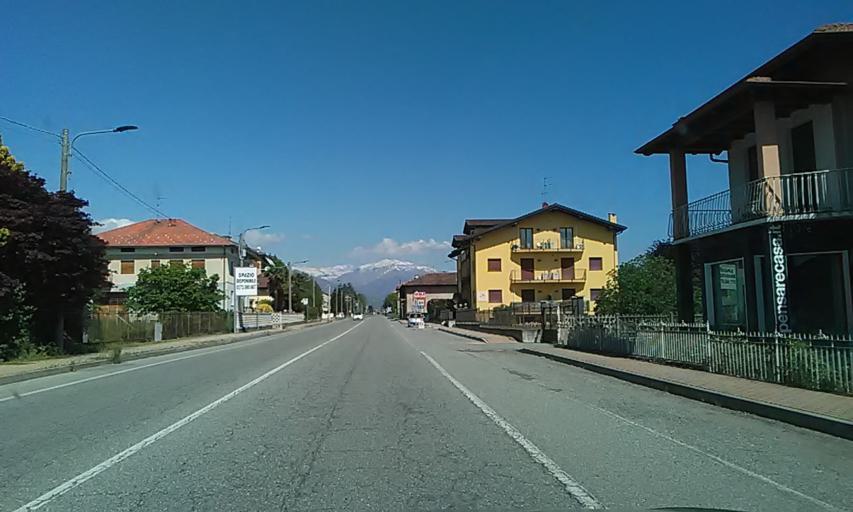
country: IT
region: Piedmont
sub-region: Provincia di Biella
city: Vergnasco
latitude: 45.4932
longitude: 8.0876
